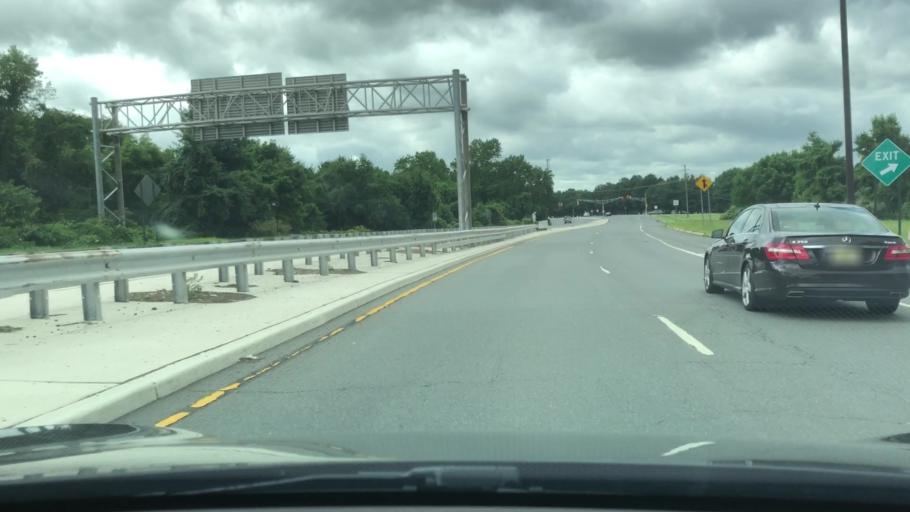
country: US
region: New Jersey
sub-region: Mercer County
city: Lawrenceville
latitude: 40.2964
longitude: -74.6785
